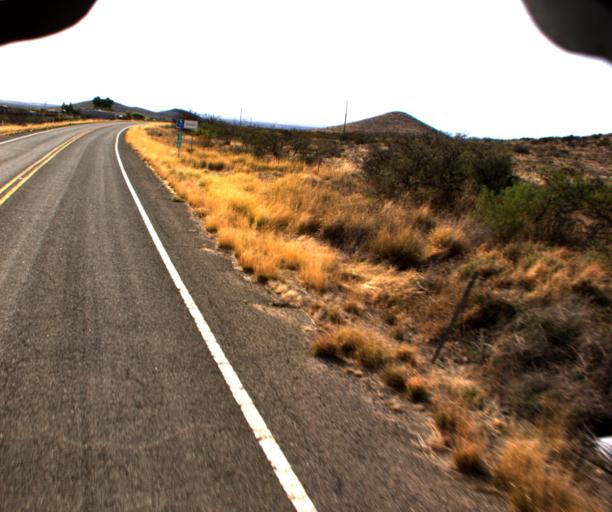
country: US
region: Arizona
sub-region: Cochise County
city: Willcox
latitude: 32.1819
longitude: -109.6596
